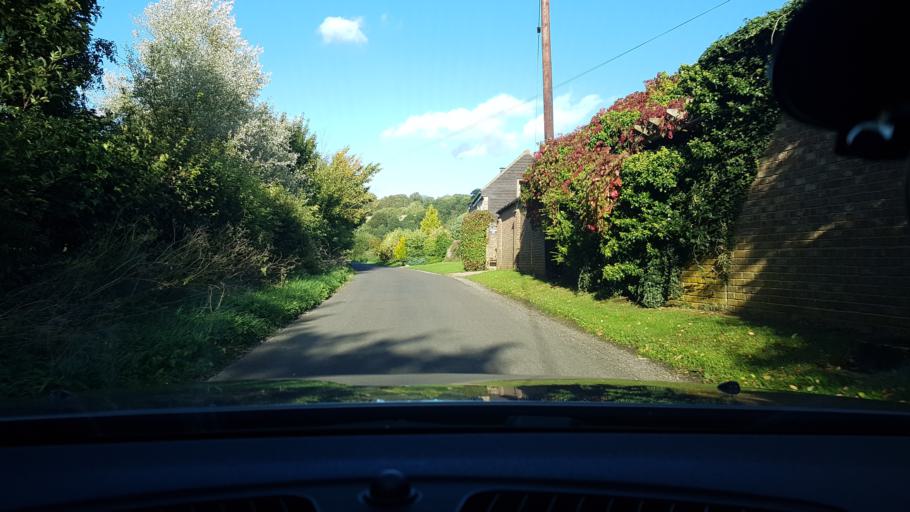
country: GB
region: England
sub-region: Wiltshire
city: Ramsbury
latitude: 51.4521
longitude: -1.5800
